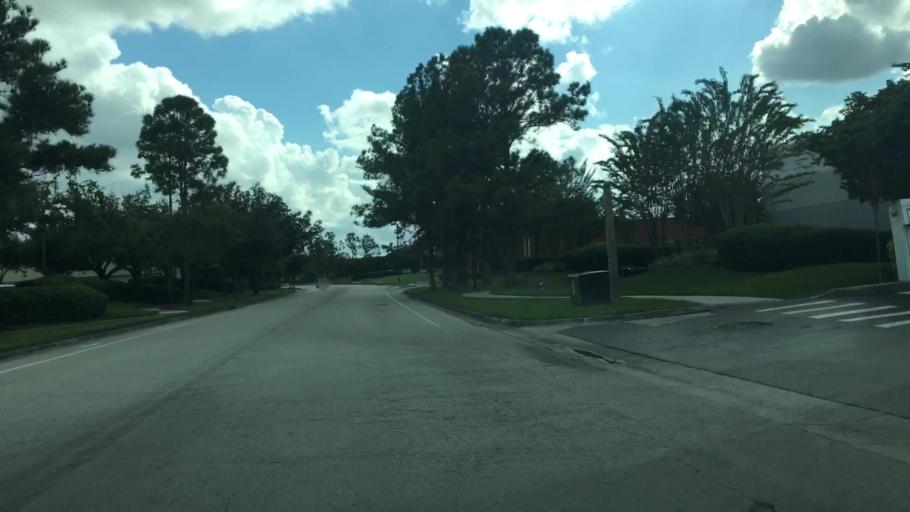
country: US
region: Florida
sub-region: Orange County
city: Conway
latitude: 28.4615
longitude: -81.2962
